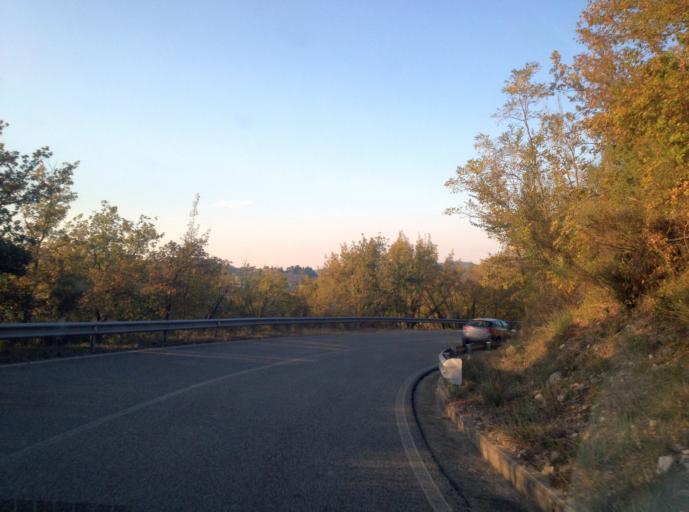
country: IT
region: Tuscany
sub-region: Provincia di Siena
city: Castellina in Chianti
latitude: 43.5066
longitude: 11.2923
